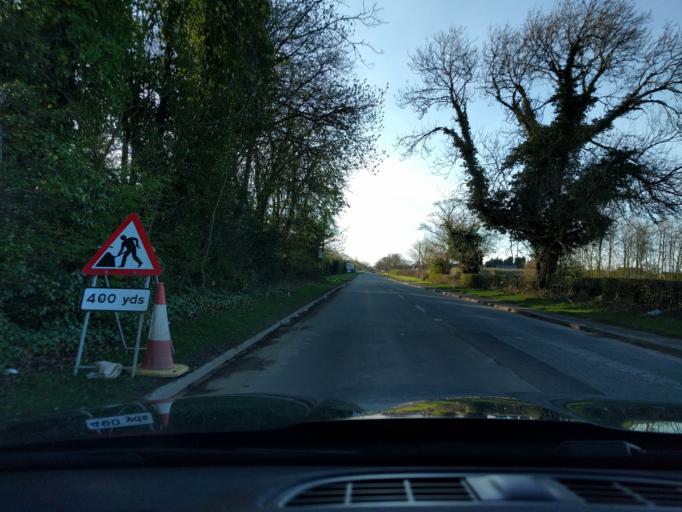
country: GB
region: England
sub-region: Northumberland
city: Morpeth
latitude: 55.1540
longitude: -1.6703
